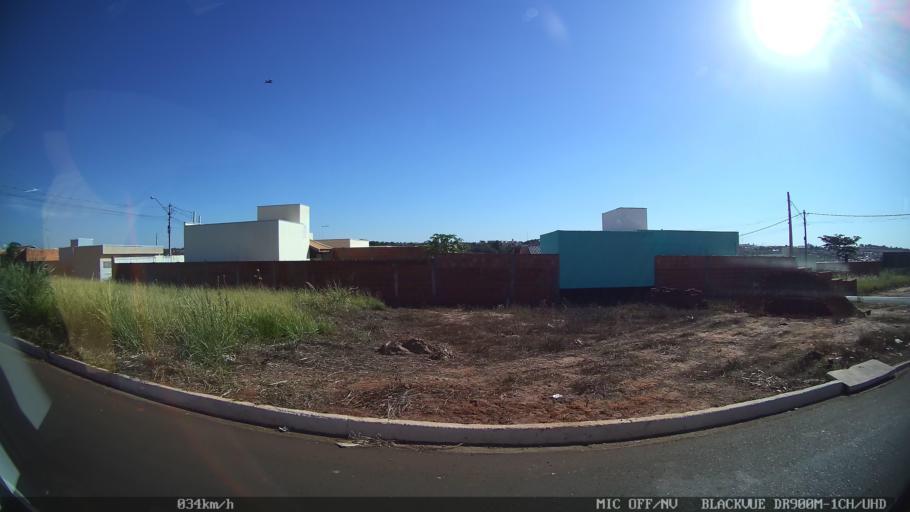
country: BR
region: Sao Paulo
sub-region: Olimpia
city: Olimpia
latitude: -20.7383
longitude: -48.8826
